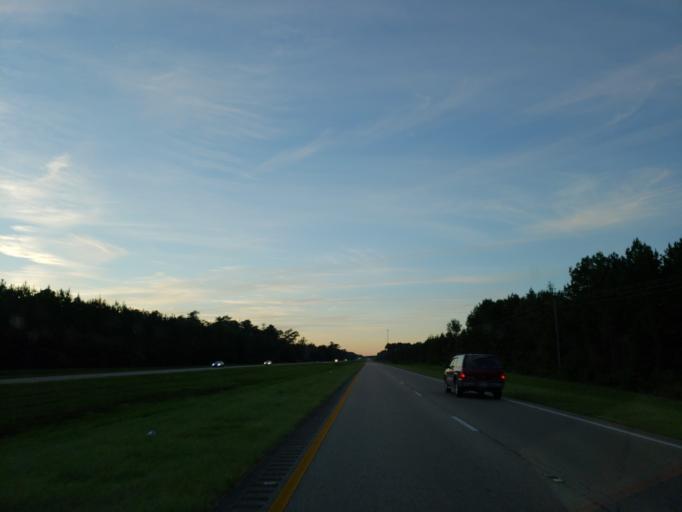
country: US
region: Mississippi
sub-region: Wayne County
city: Belmont
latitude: 31.6046
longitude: -88.5613
